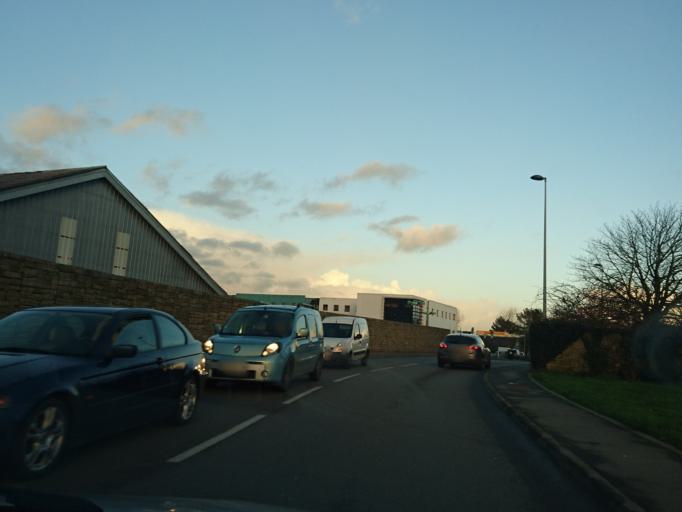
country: FR
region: Brittany
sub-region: Departement du Finistere
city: Gouesnou
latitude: 48.4318
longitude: -4.4649
